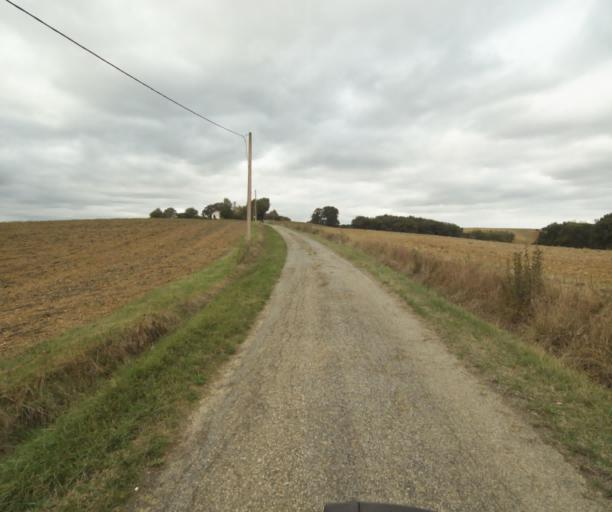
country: FR
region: Midi-Pyrenees
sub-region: Departement du Tarn-et-Garonne
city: Beaumont-de-Lomagne
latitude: 43.8488
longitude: 1.0698
